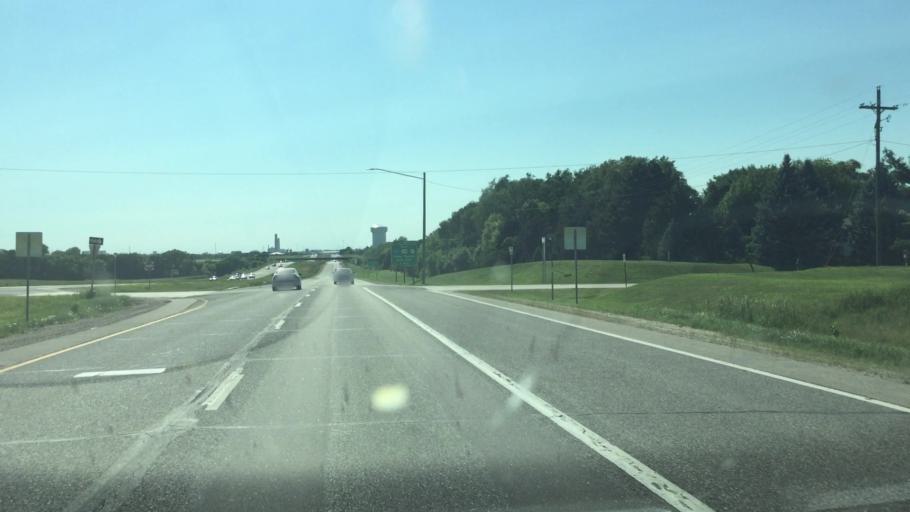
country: US
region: Iowa
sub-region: Linn County
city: Ely
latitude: 41.9266
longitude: -91.6238
